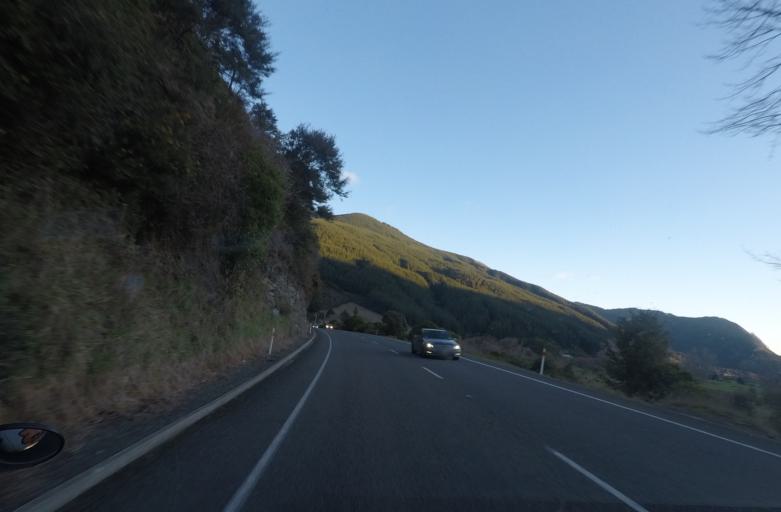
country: NZ
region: Marlborough
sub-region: Marlborough District
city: Picton
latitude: -41.2784
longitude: 173.7284
